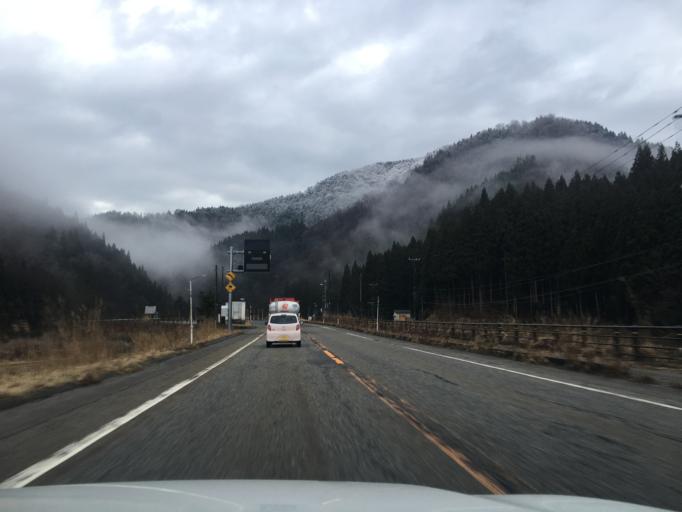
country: JP
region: Niigata
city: Murakami
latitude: 38.4604
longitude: 139.5741
